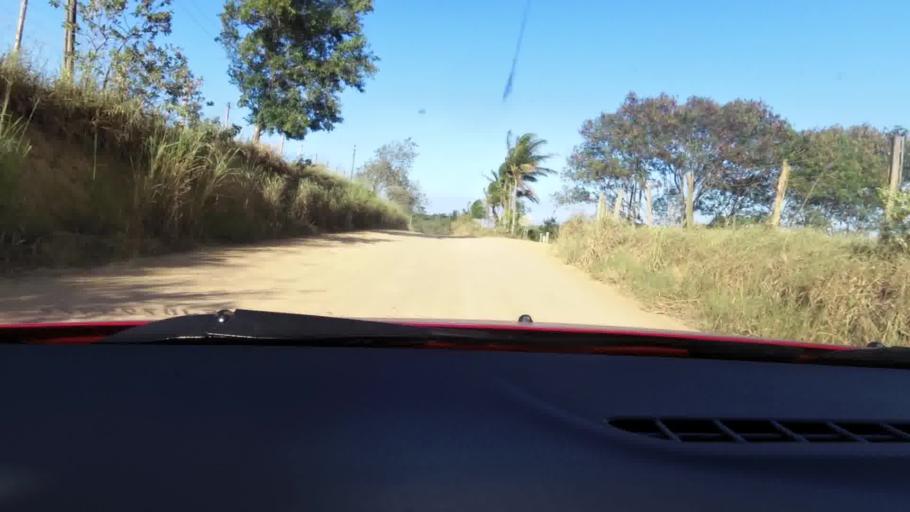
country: BR
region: Espirito Santo
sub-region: Guarapari
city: Guarapari
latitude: -20.5371
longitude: -40.4455
